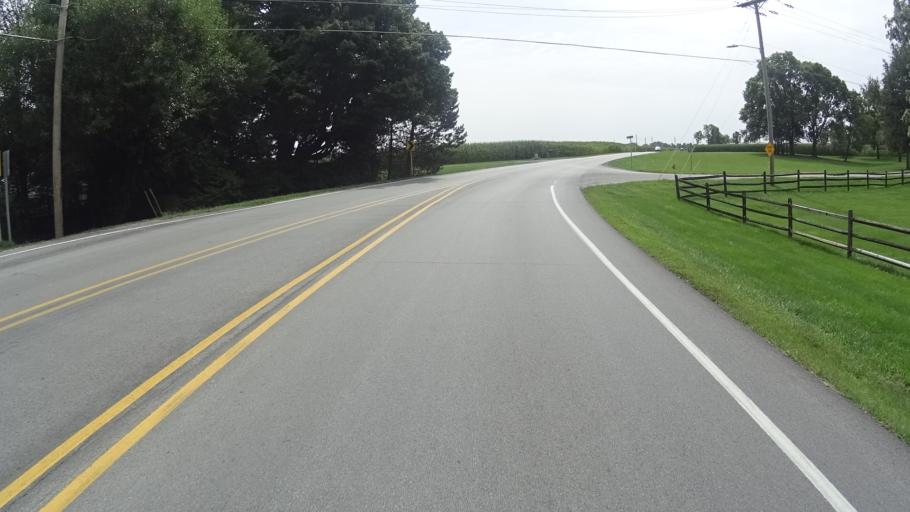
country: US
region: Indiana
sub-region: Madison County
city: Pendleton
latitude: 40.0094
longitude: -85.7875
